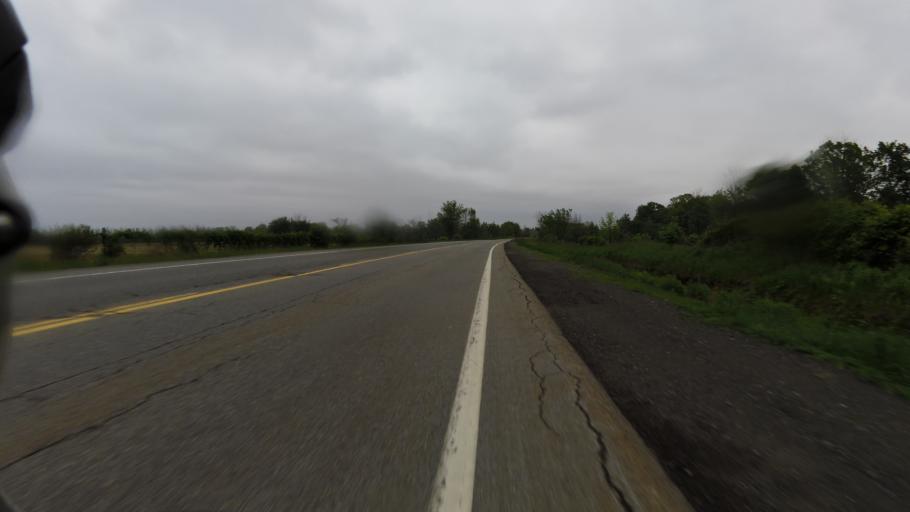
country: CA
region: Ontario
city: Bells Corners
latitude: 45.3248
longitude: -75.8446
